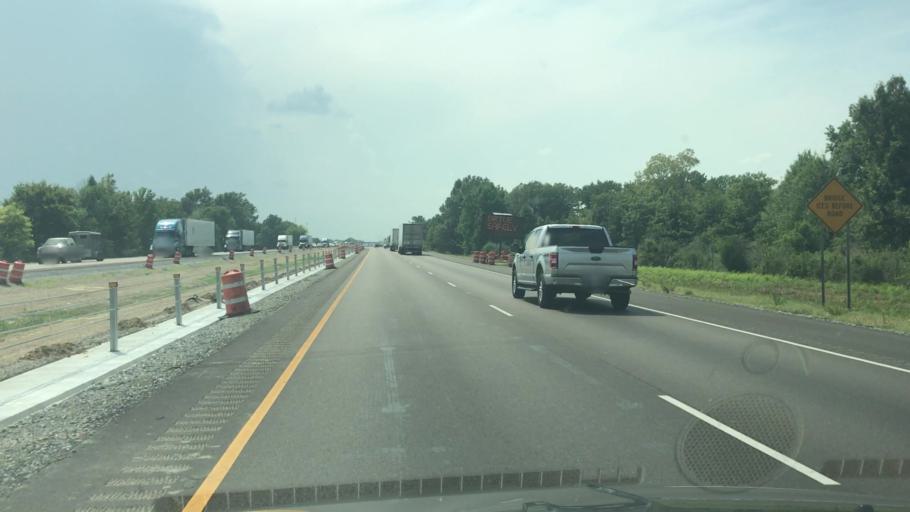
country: US
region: Arkansas
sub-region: Crittenden County
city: Earle
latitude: 35.1340
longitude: -90.4497
